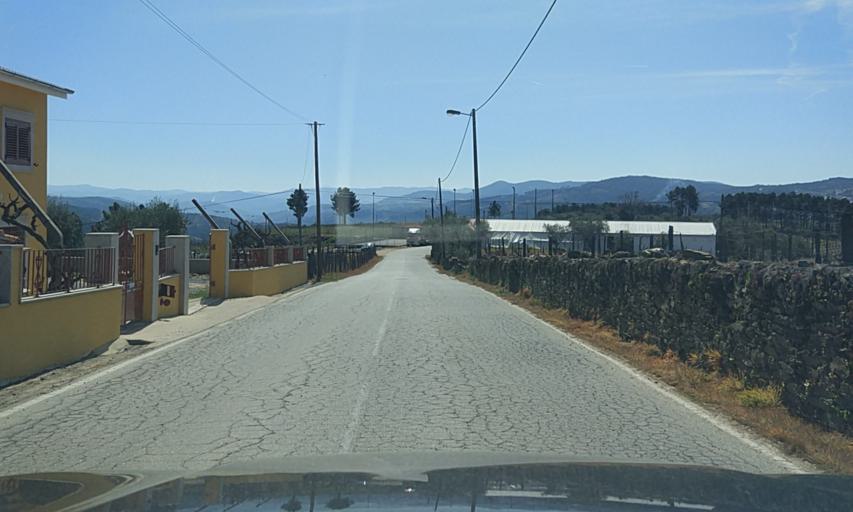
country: PT
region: Vila Real
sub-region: Sabrosa
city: Sabrosa
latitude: 41.3232
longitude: -7.5552
